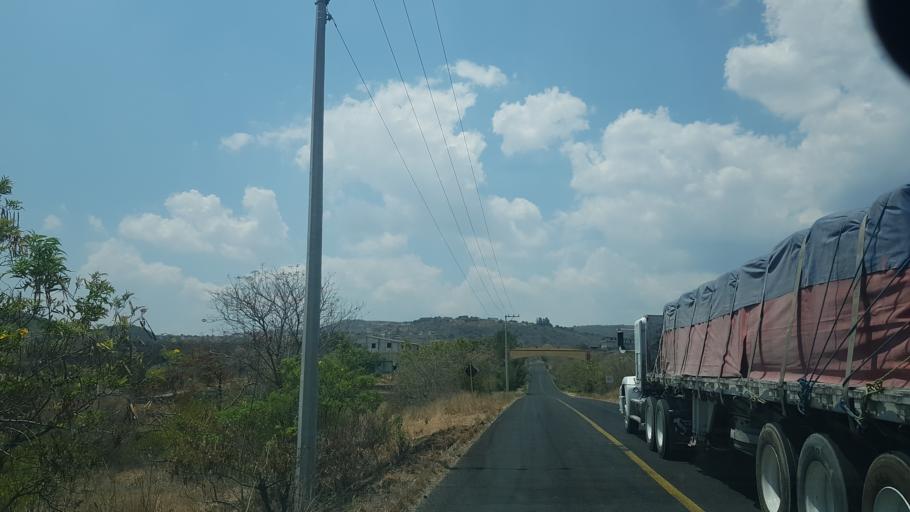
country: MX
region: Puebla
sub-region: Atzitzihuacan
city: Santiago Atzitzihuacan
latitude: 18.8321
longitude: -98.5899
